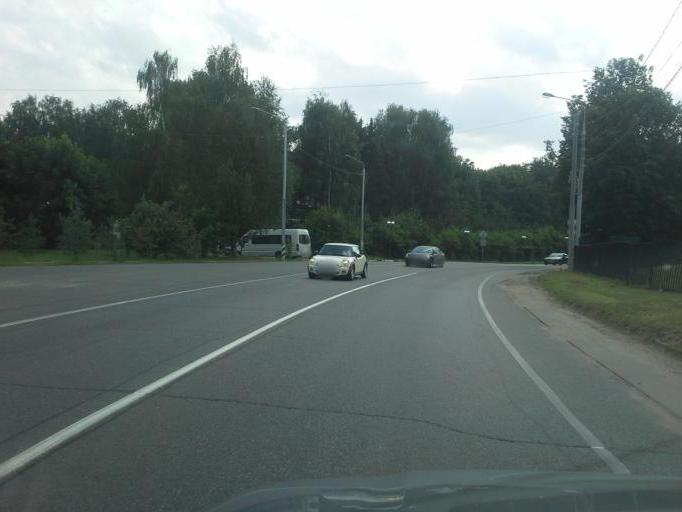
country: RU
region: Moskovskaya
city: Barvikha
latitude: 55.7252
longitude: 37.2788
